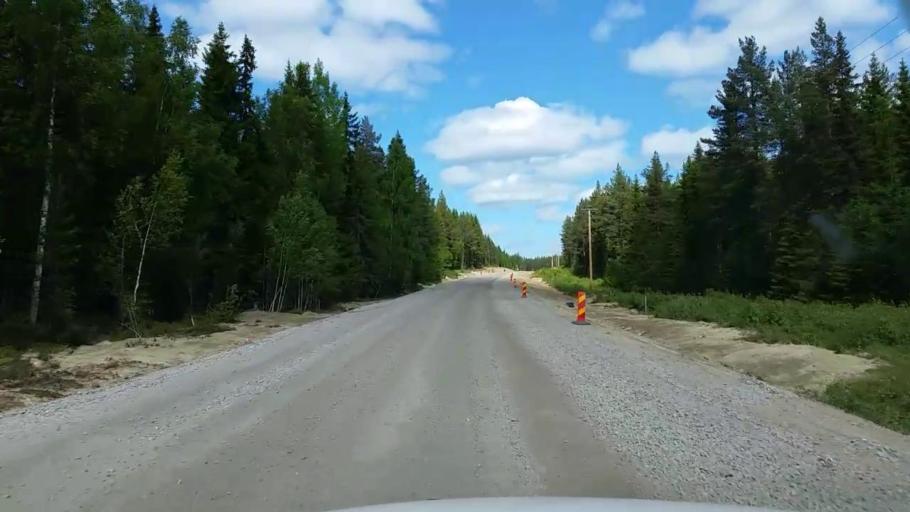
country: SE
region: Gaevleborg
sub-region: Ovanakers Kommun
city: Edsbyn
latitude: 61.5831
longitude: 15.9059
